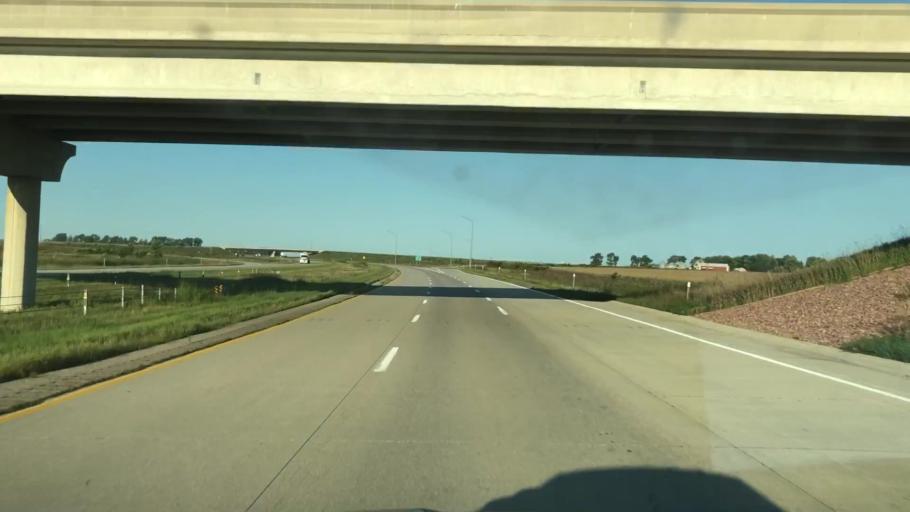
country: US
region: Iowa
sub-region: Osceola County
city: Sibley
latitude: 43.3845
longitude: -95.7414
